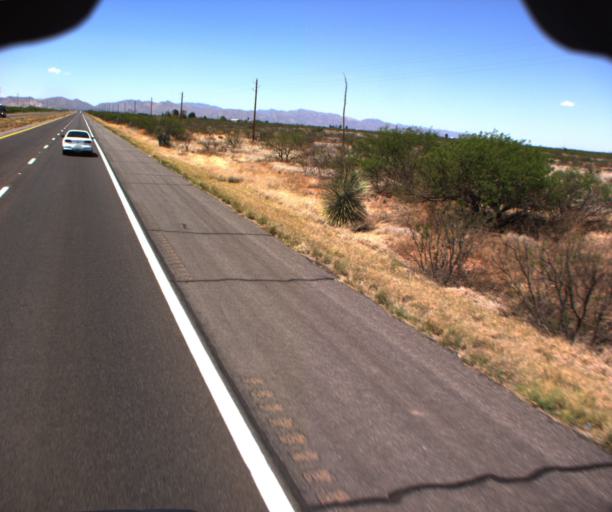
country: US
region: Arizona
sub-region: Cochise County
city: Pirtleville
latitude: 31.3582
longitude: -109.6395
